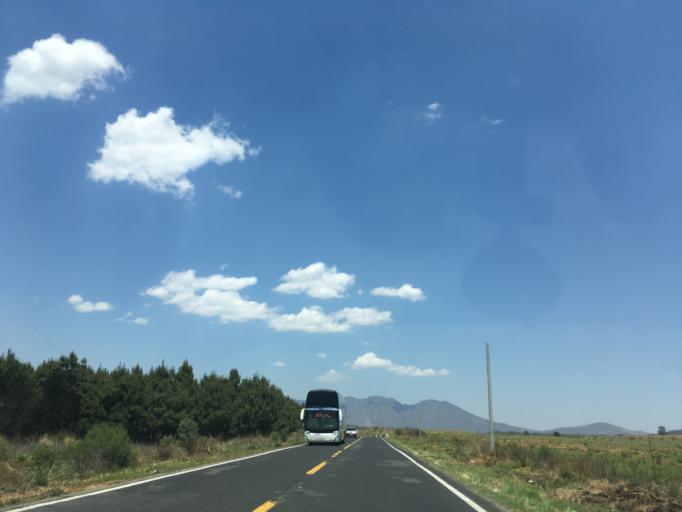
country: MX
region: Mexico
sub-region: Chalco
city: Zopoco
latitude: 19.7887
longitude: -102.0234
